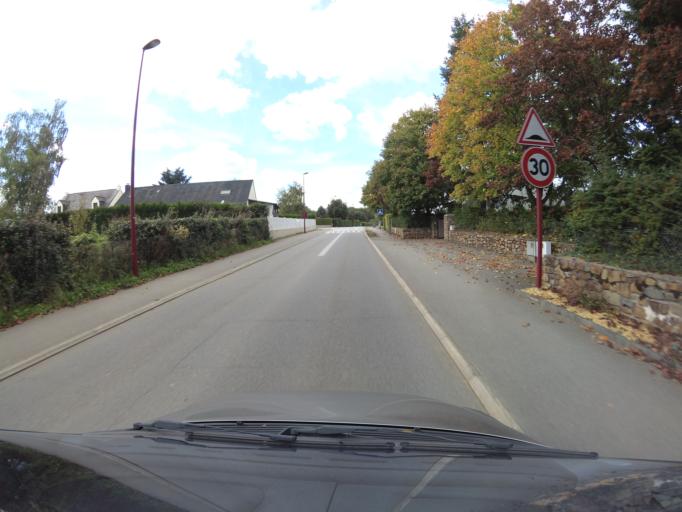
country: FR
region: Pays de la Loire
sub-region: Departement de la Loire-Atlantique
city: Suce-sur-Erdre
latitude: 47.3467
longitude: -1.5327
